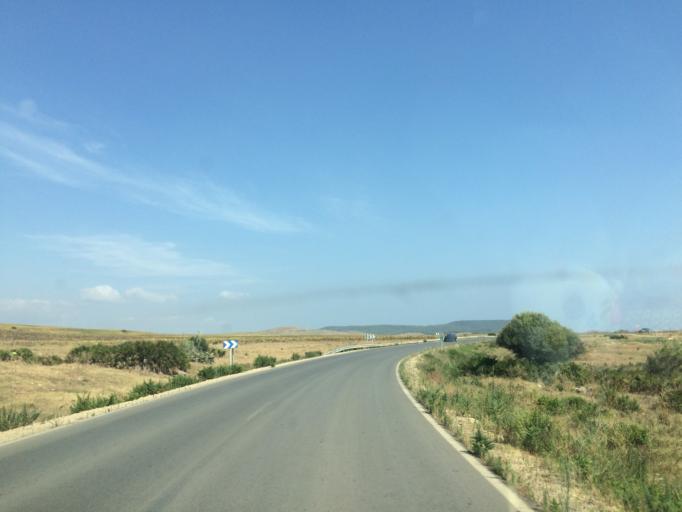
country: ES
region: Andalusia
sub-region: Provincia de Cadiz
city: Conil de la Frontera
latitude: 36.2345
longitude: -6.0487
